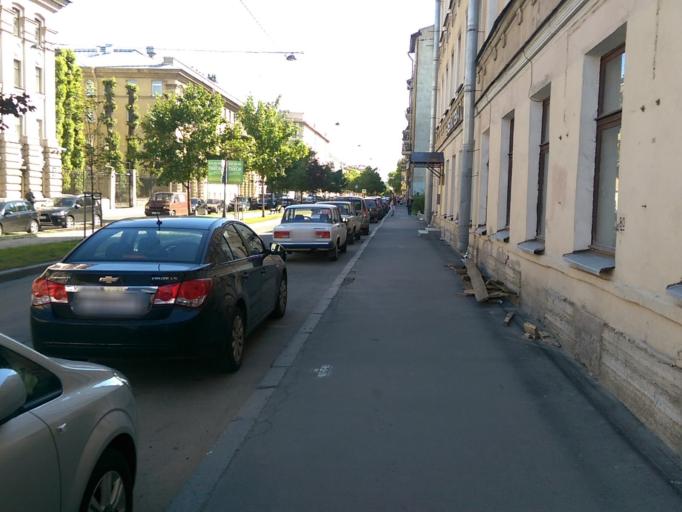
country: RU
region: St.-Petersburg
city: Saint Petersburg
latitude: 59.9112
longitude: 30.3189
